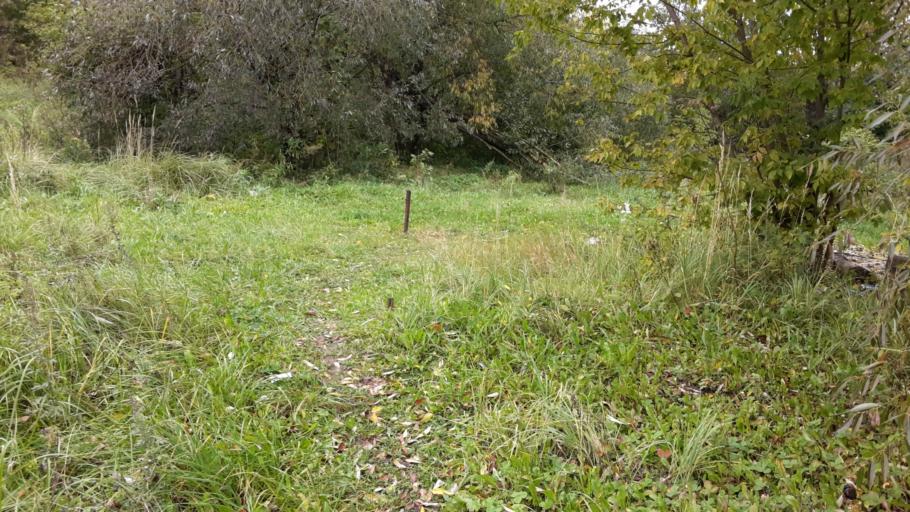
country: RU
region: Moscow
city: Orekhovo-Borisovo Severnoye
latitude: 55.6337
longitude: 37.6877
